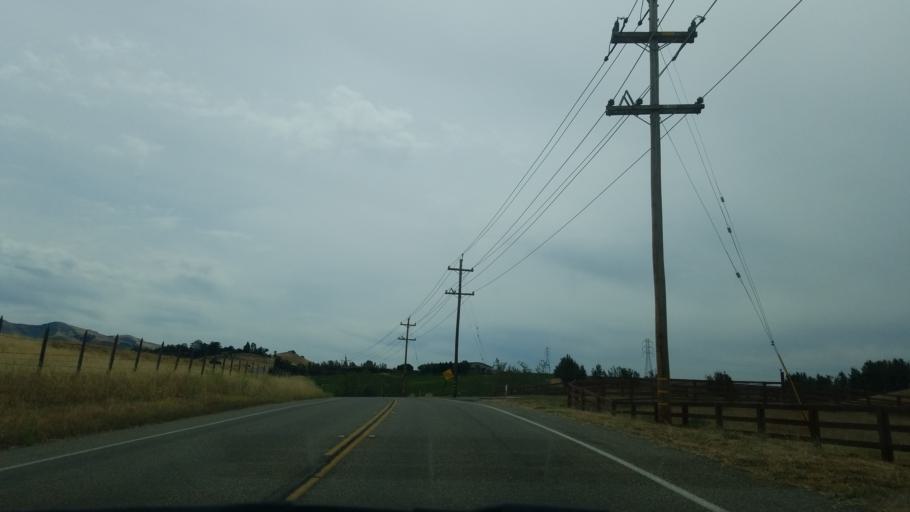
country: US
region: California
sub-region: San Luis Obispo County
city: San Luis Obispo
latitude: 35.2441
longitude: -120.6140
